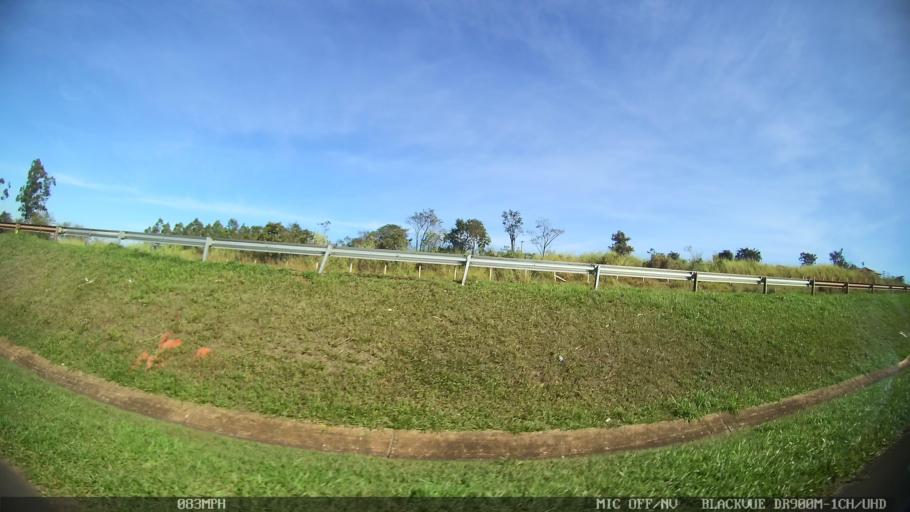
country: BR
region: Sao Paulo
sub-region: Pirassununga
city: Pirassununga
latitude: -22.0903
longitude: -47.4186
